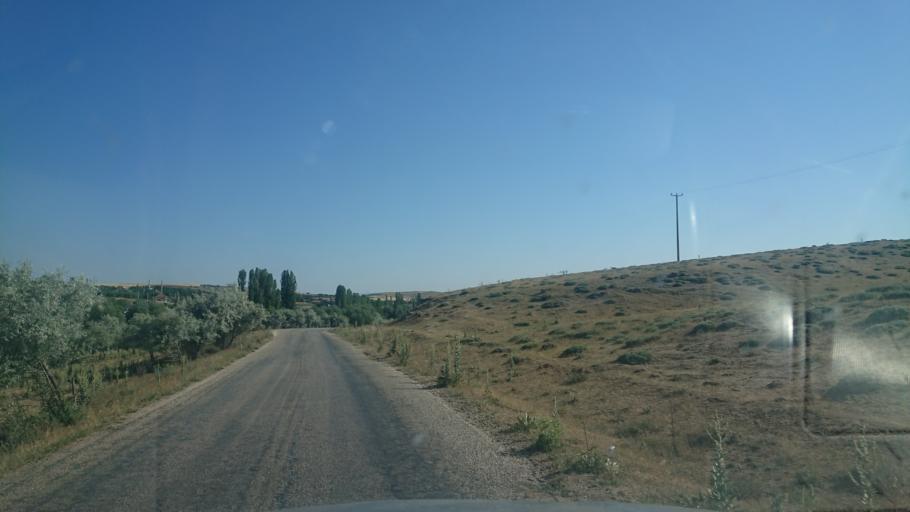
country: TR
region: Aksaray
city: Agacoren
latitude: 38.8773
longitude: 33.8808
